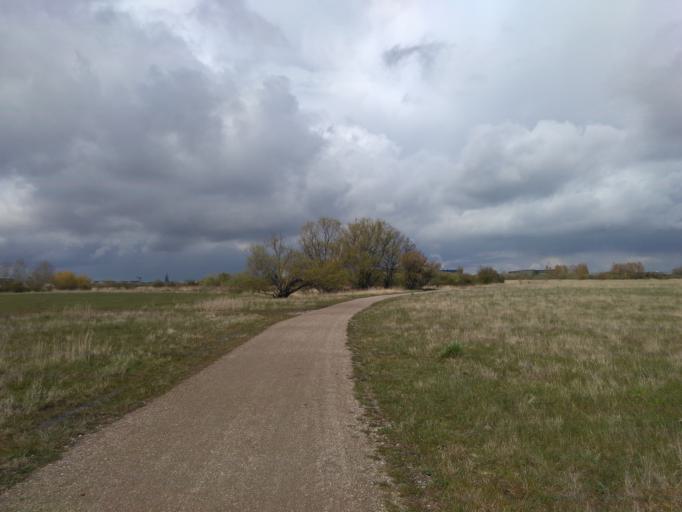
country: DK
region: Capital Region
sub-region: Kobenhavn
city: Copenhagen
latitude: 55.6441
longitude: 12.5700
